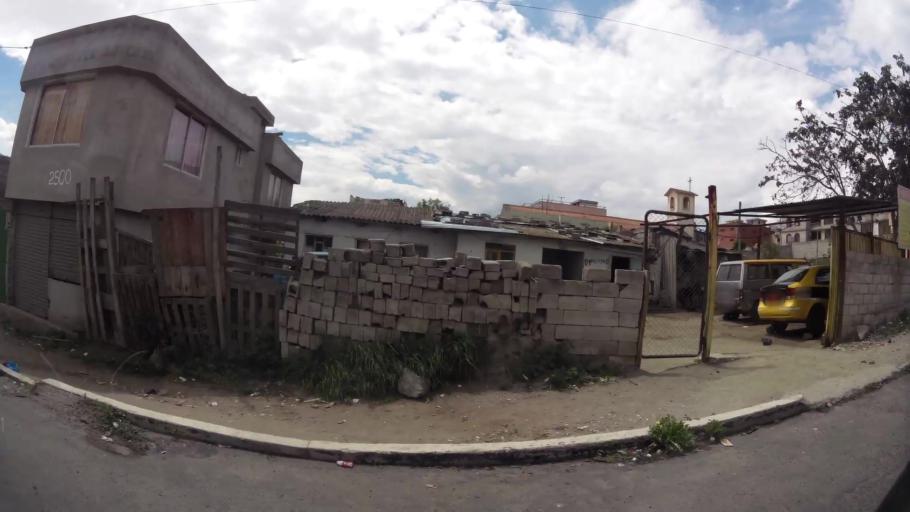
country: EC
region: Pichincha
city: Quito
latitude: -0.0809
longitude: -78.4114
